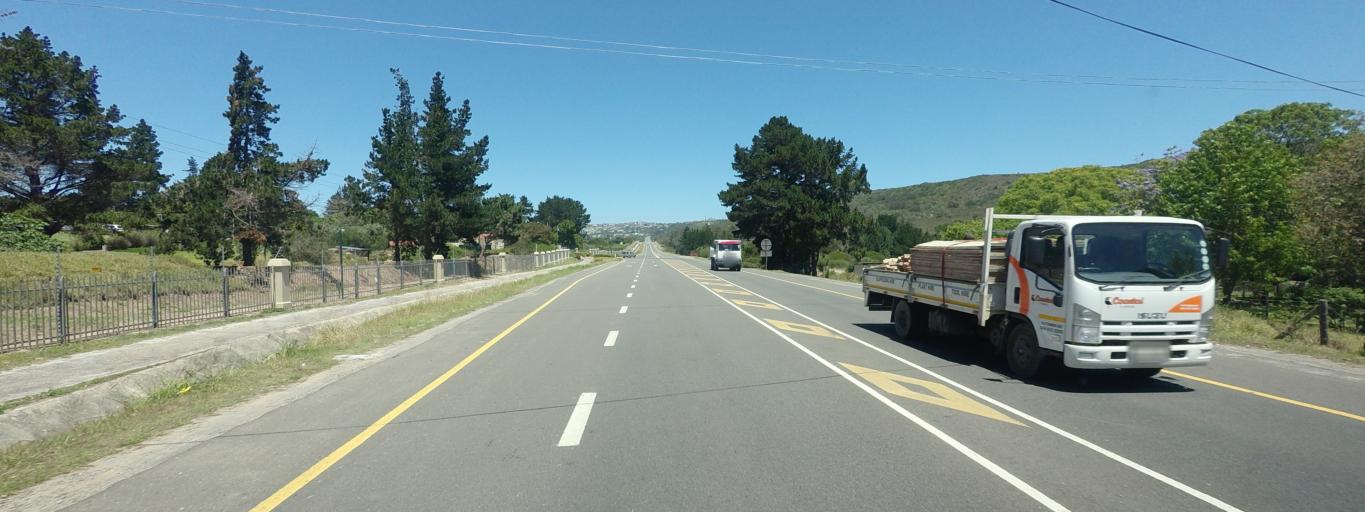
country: ZA
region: Western Cape
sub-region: Eden District Municipality
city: Plettenberg Bay
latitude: -34.0251
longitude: 23.3799
